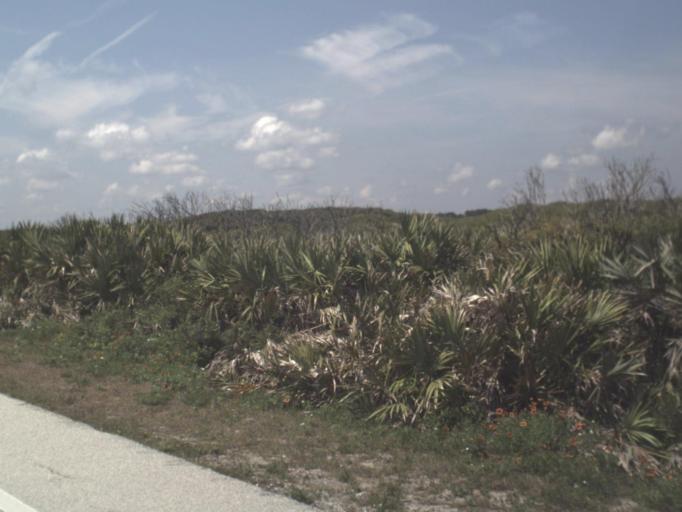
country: US
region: Florida
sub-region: Saint Johns County
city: Palm Valley
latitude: 30.0870
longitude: -81.3383
